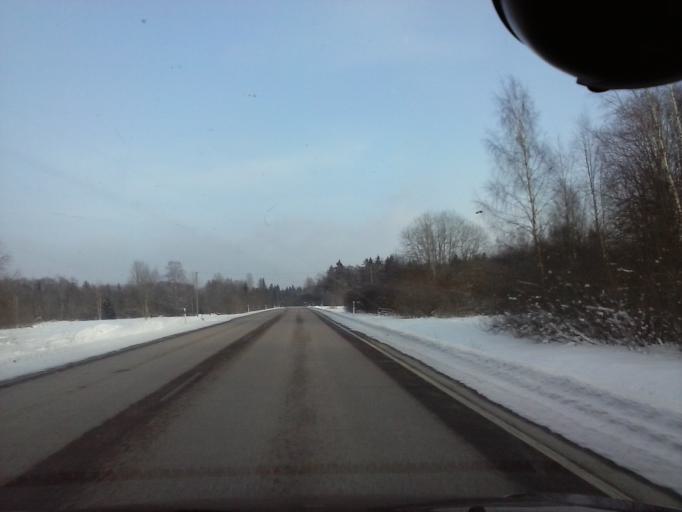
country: EE
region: Jogevamaa
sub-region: Poltsamaa linn
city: Poltsamaa
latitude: 58.4062
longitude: 25.9926
